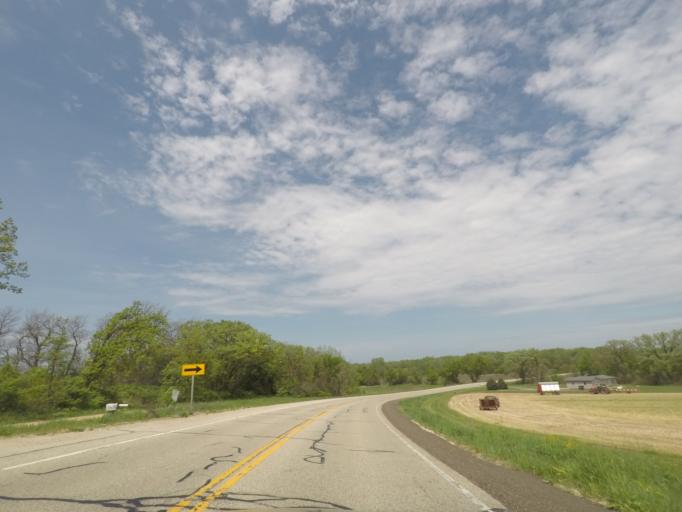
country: US
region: Wisconsin
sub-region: Rock County
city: Orfordville
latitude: 42.6493
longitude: -89.2875
